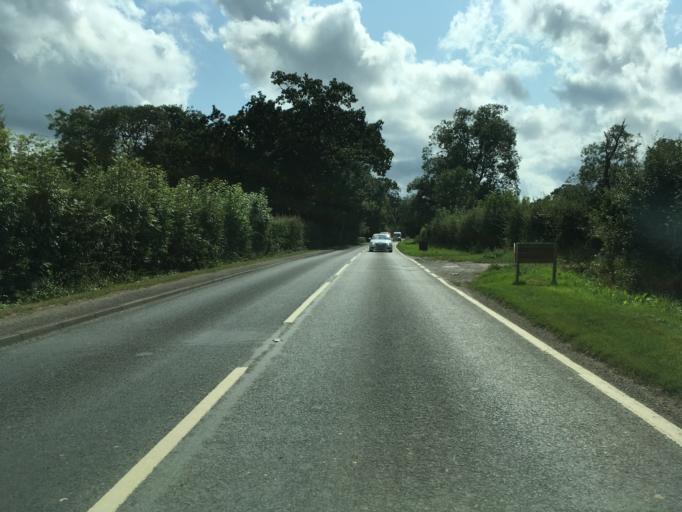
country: GB
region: England
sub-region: Kent
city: Headcorn
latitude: 51.1217
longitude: 0.6469
